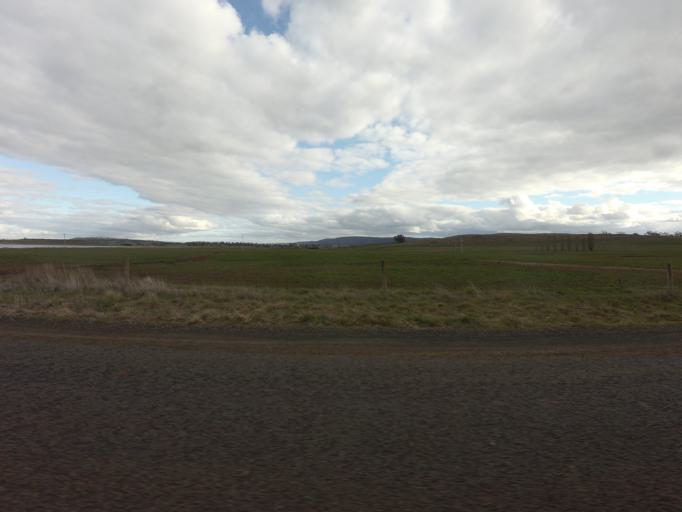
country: AU
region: Tasmania
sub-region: Northern Midlands
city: Evandale
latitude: -41.9135
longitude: 147.4699
